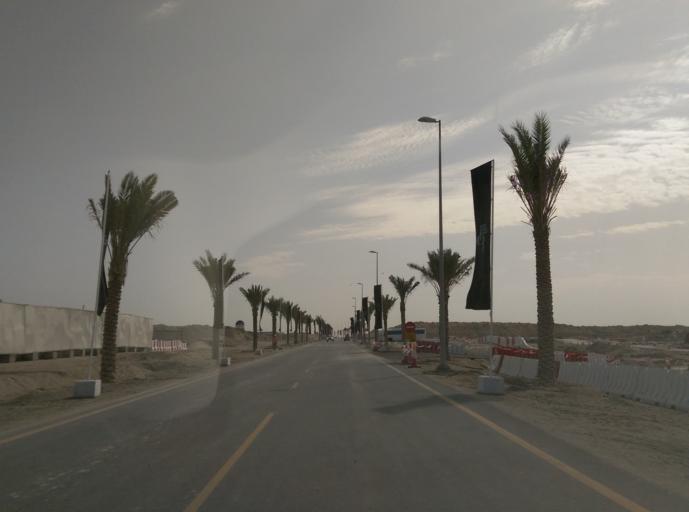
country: AE
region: Dubai
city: Dubai
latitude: 25.1875
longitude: 55.3039
